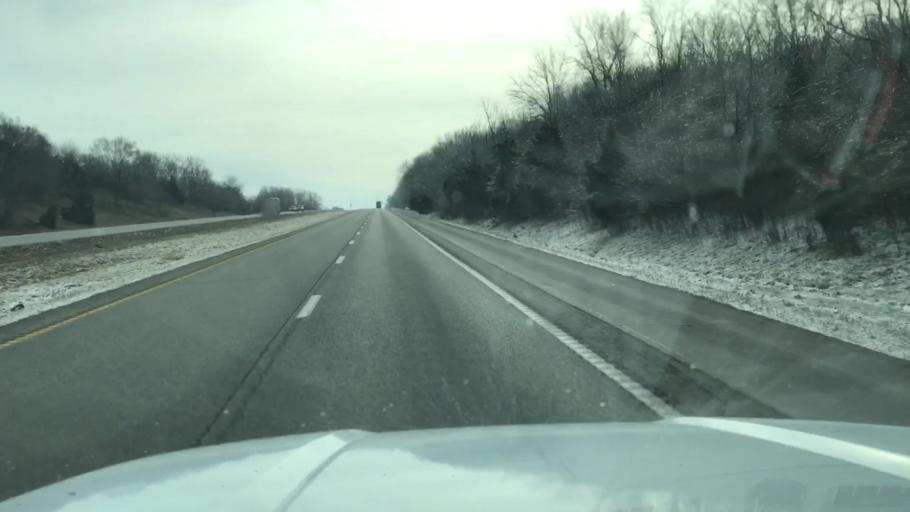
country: US
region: Missouri
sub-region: Andrew County
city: Savannah
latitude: 39.8996
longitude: -94.8783
